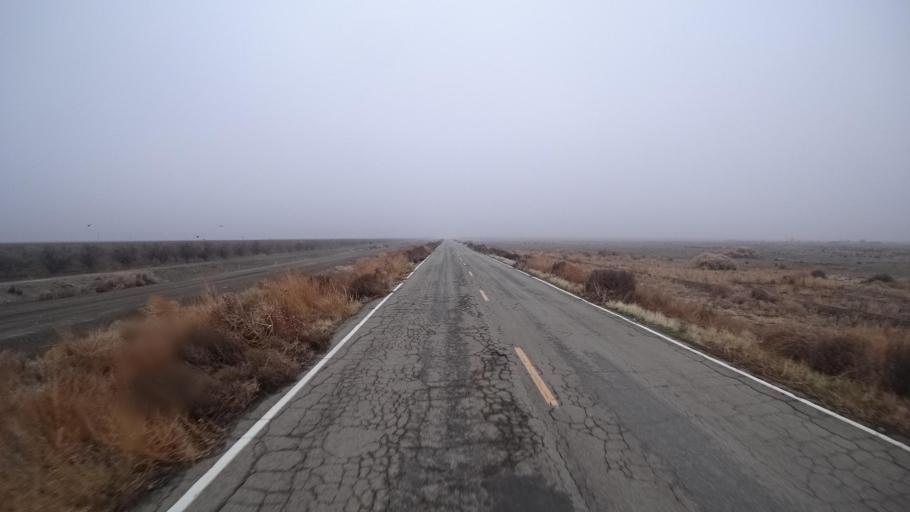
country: US
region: California
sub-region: Kern County
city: Lost Hills
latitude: 35.5914
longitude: -119.6175
